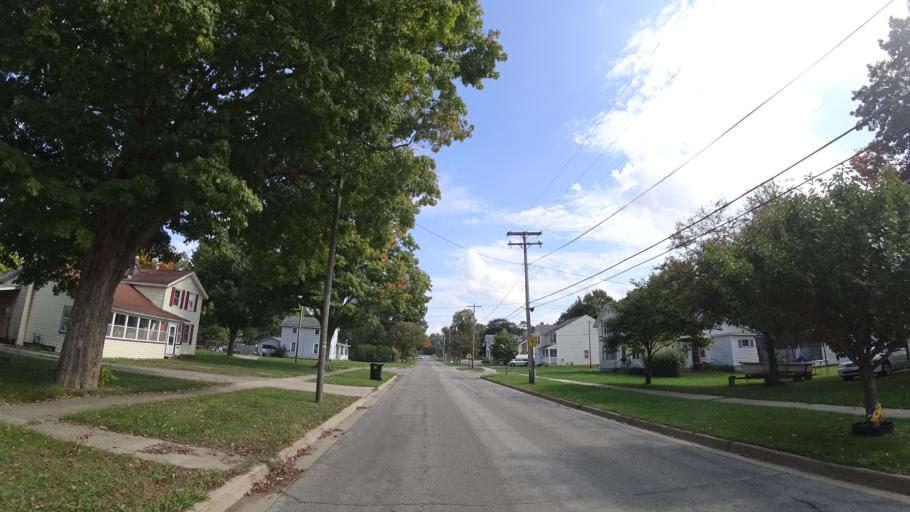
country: US
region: Michigan
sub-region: Saint Joseph County
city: Three Rivers
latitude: 41.9332
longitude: -85.6262
